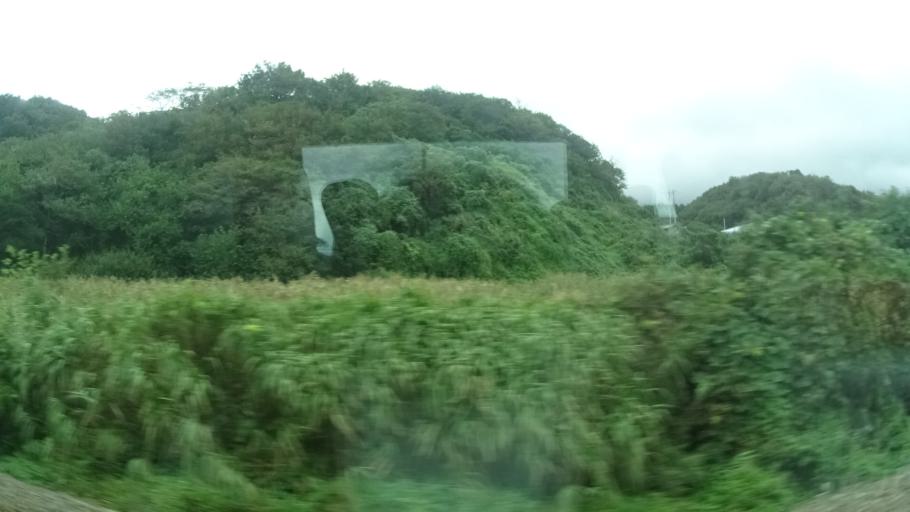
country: JP
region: Yamagata
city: Tsuruoka
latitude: 38.5752
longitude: 139.5588
